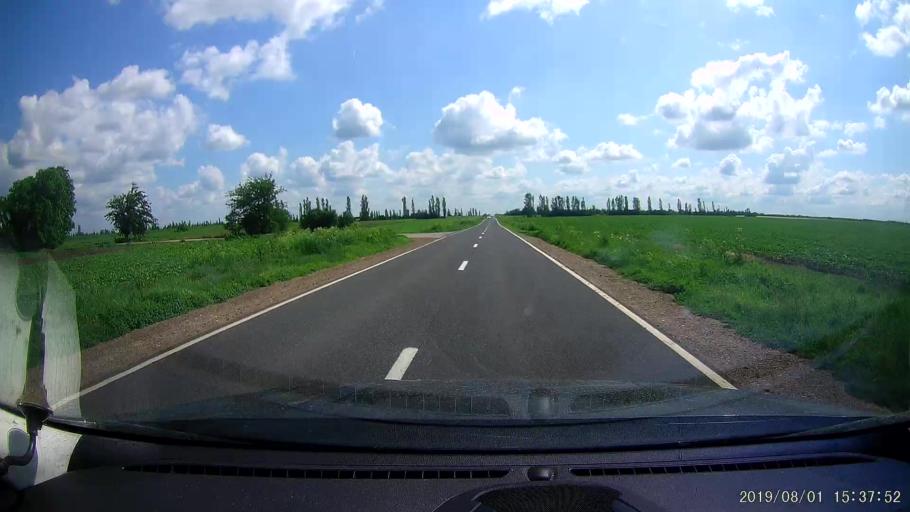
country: RO
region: Braila
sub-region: Comuna Insuratei
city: Insuratei
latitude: 44.8948
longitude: 27.5841
